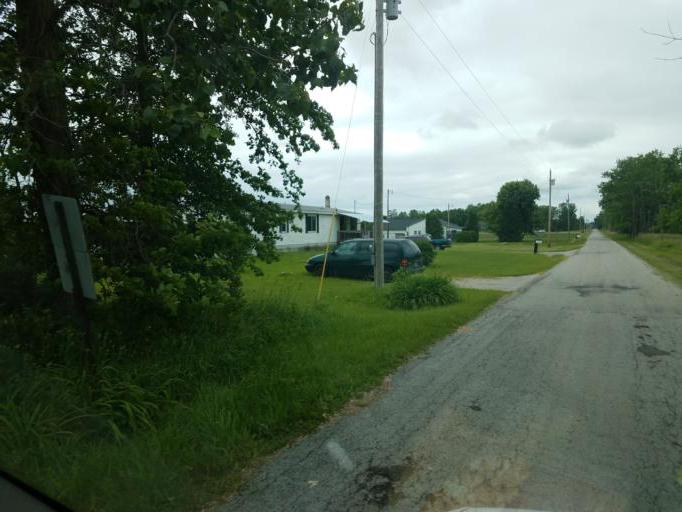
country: US
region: Ohio
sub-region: Morrow County
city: Cardington
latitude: 40.5434
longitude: -82.9575
